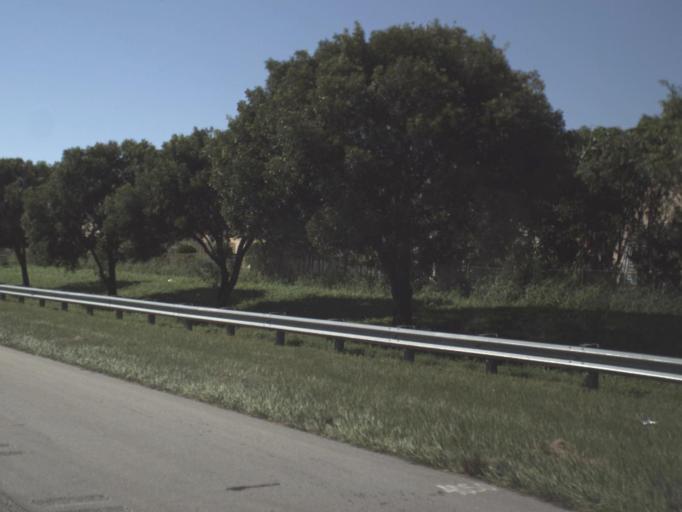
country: US
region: Florida
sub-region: Miami-Dade County
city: Goulds
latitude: 25.5460
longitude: -80.3629
